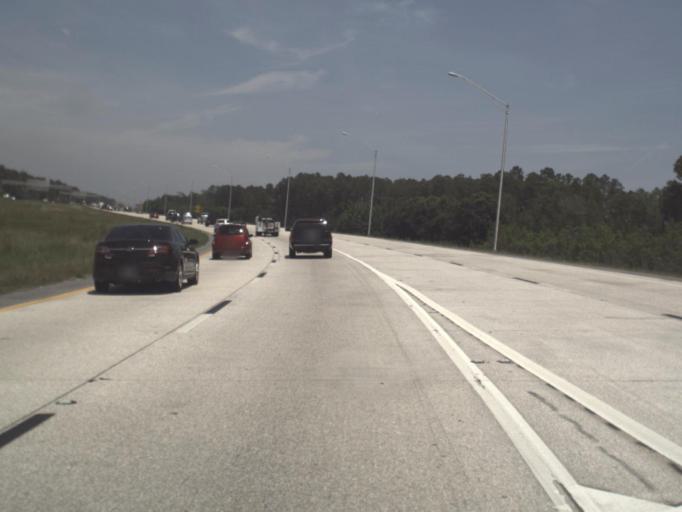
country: US
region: Florida
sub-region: Saint Johns County
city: Palm Valley
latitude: 30.1805
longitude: -81.5131
